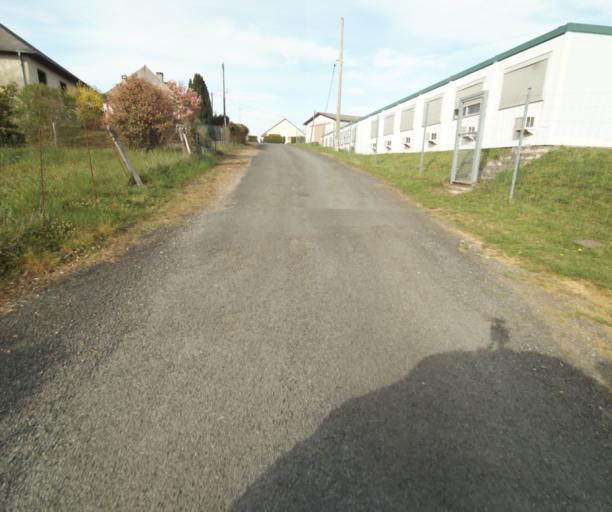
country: FR
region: Limousin
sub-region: Departement de la Correze
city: Naves
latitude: 45.3211
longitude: 1.7591
